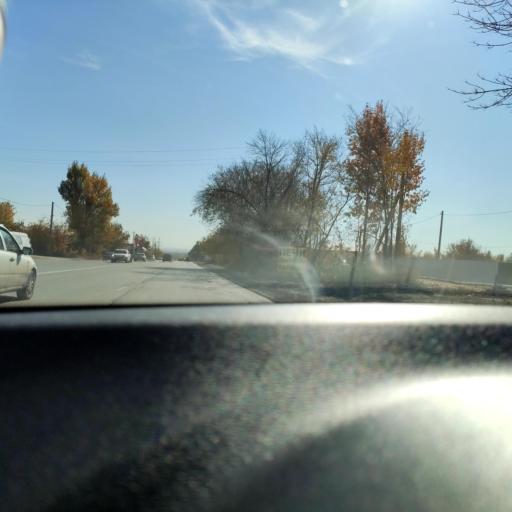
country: RU
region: Samara
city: Petra-Dubrava
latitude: 53.2662
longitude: 50.2830
